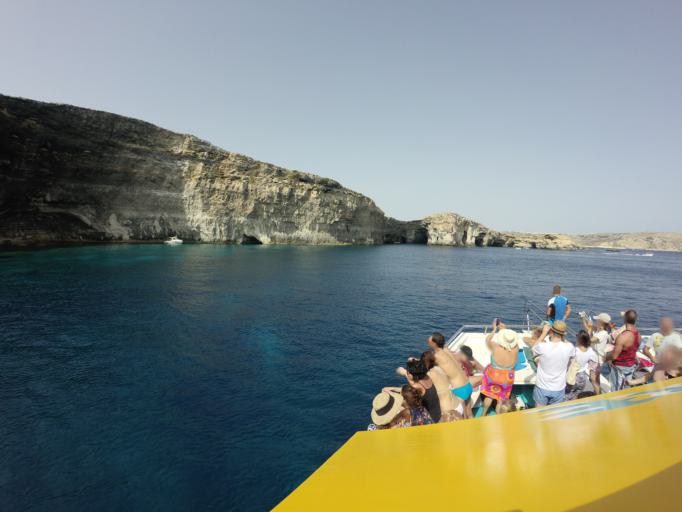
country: MT
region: Il-Qala
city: Qala
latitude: 36.0164
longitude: 14.3434
